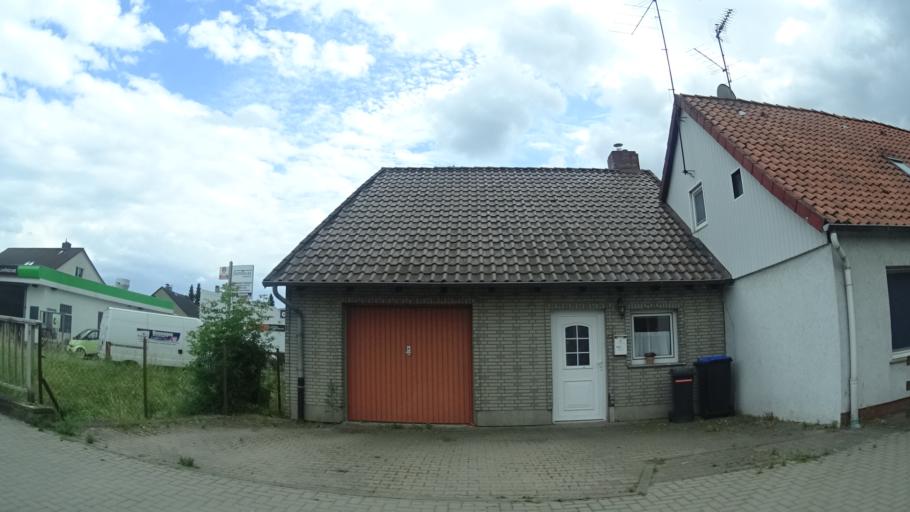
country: DE
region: Lower Saxony
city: Elze
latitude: 52.1713
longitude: 9.6713
